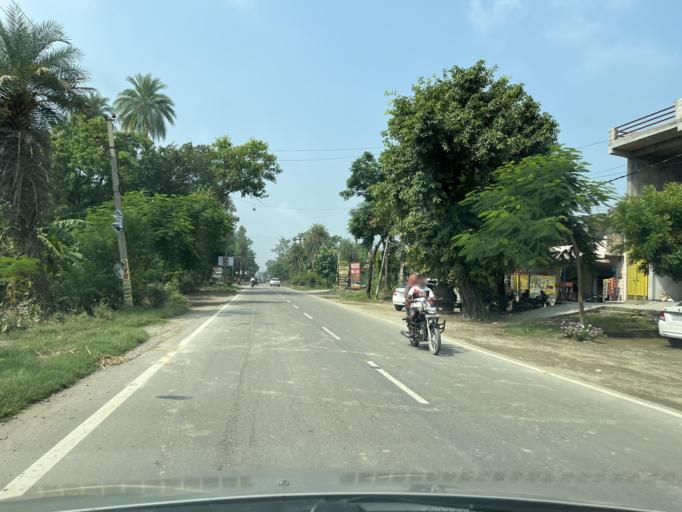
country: IN
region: Uttarakhand
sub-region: Udham Singh Nagar
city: Bazpur
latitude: 29.1699
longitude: 79.1650
